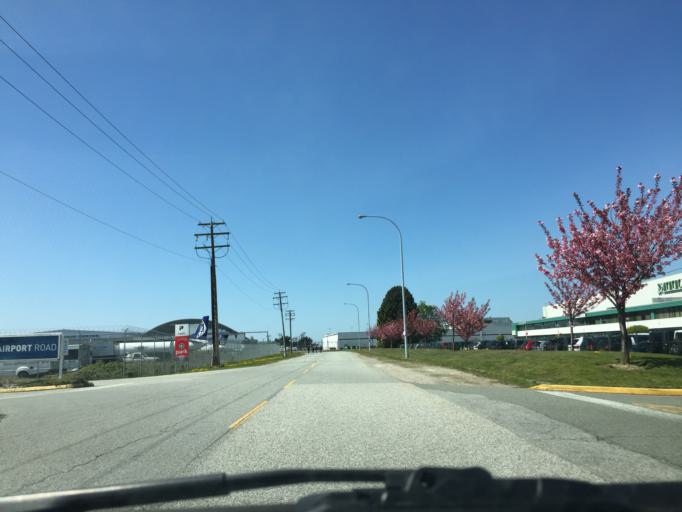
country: CA
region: British Columbia
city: Richmond
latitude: 49.1800
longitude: -123.1596
